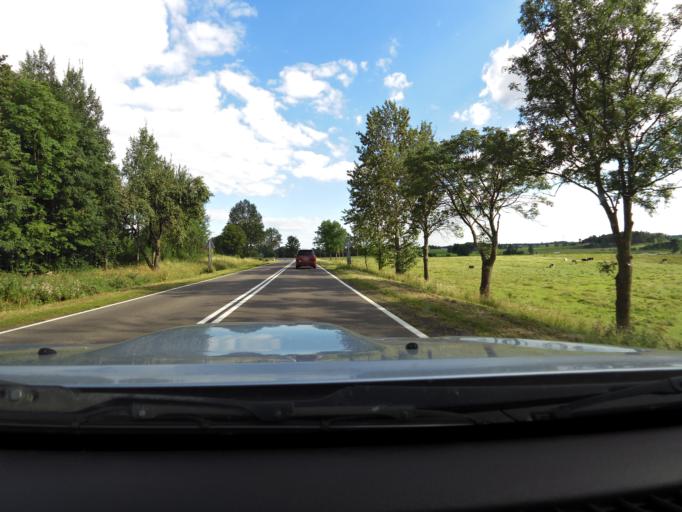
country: PL
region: Podlasie
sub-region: Powiat grajewski
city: Rajgrod
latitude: 53.8663
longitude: 22.6809
